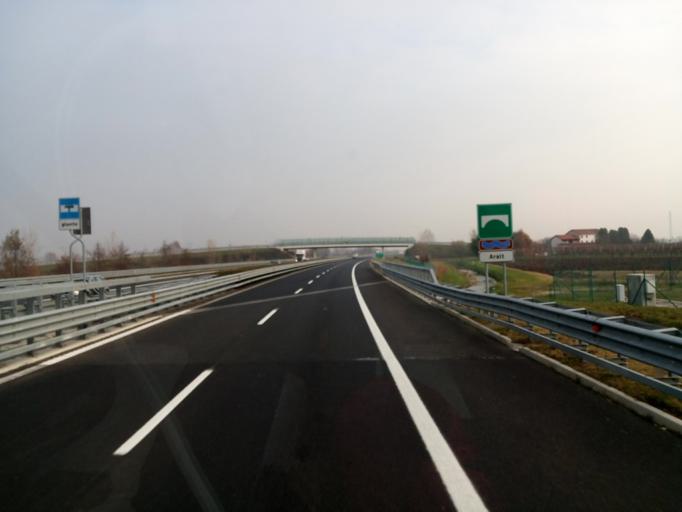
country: IT
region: Veneto
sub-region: Provincia di Treviso
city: Bibano
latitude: 45.9154
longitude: 12.4582
